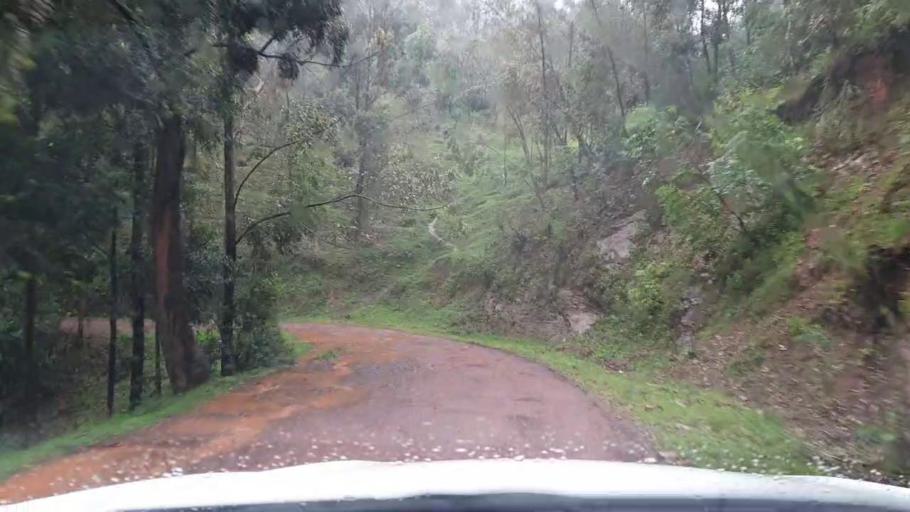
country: RW
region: Kigali
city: Kigali
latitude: -1.7655
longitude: 29.9944
